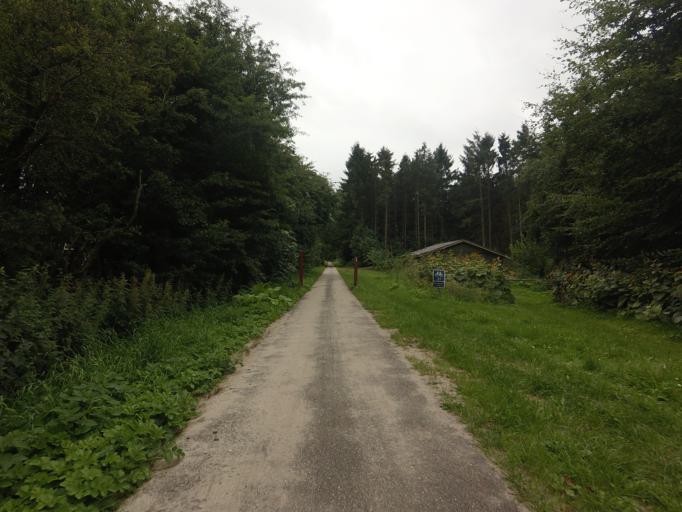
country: DK
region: Central Jutland
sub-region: Horsens Kommune
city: Braedstrup
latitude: 55.9812
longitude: 9.5959
